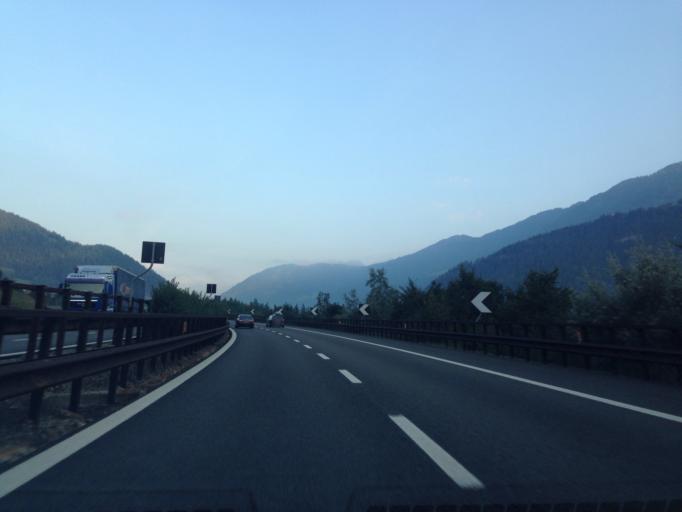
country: IT
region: Trentino-Alto Adige
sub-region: Bolzano
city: Campo di Trens
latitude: 46.8443
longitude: 11.5232
